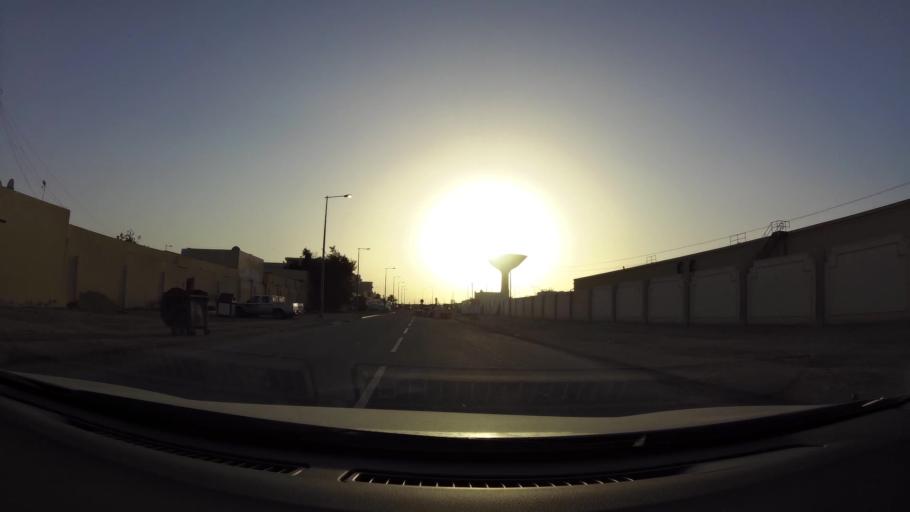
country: QA
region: Baladiyat ar Rayyan
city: Ar Rayyan
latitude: 25.3150
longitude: 51.4539
